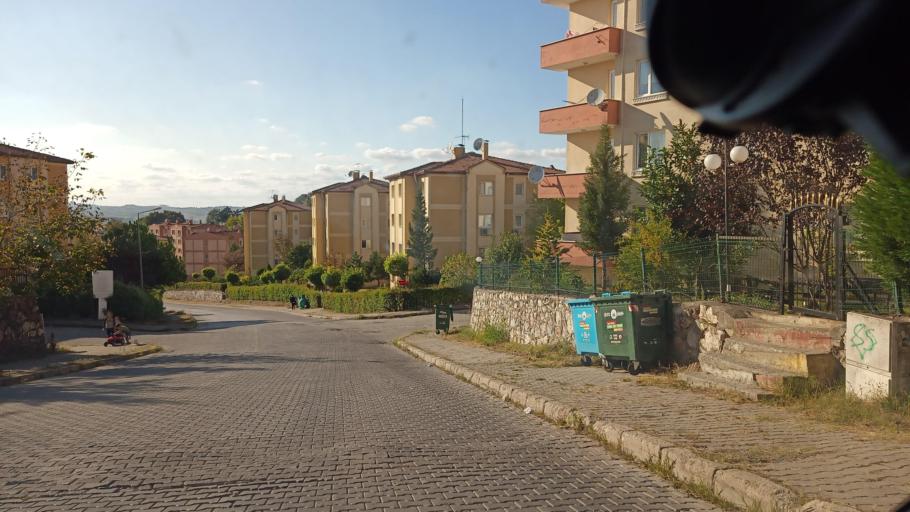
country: TR
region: Kocaeli
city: Kaymaz
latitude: 40.8612
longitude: 30.2901
